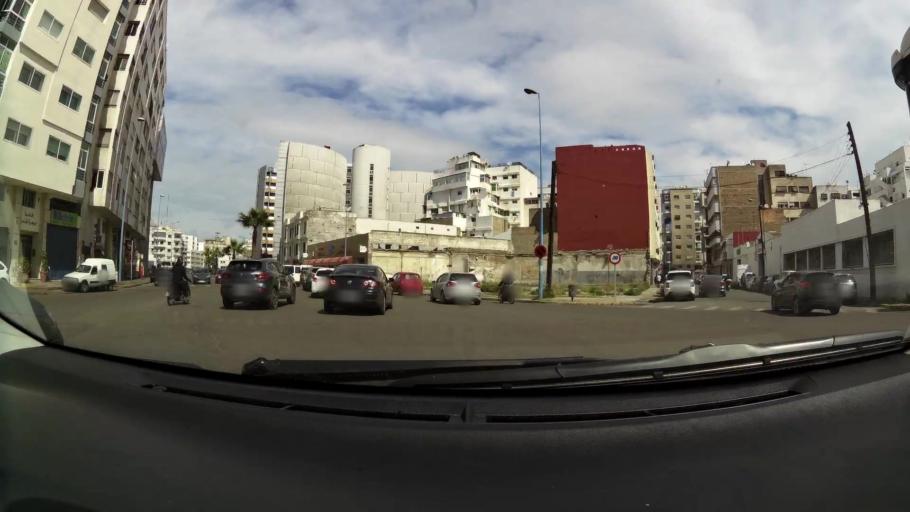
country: MA
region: Grand Casablanca
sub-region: Casablanca
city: Casablanca
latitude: 33.5892
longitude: -7.6021
